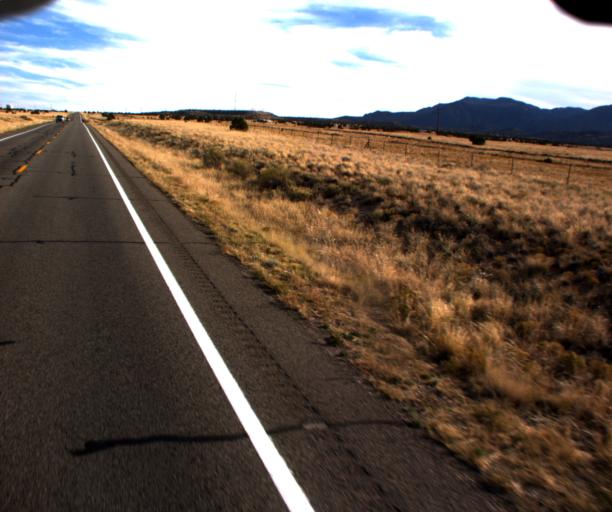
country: US
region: New Mexico
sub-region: San Juan County
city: Shiprock
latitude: 36.9074
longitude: -109.0709
